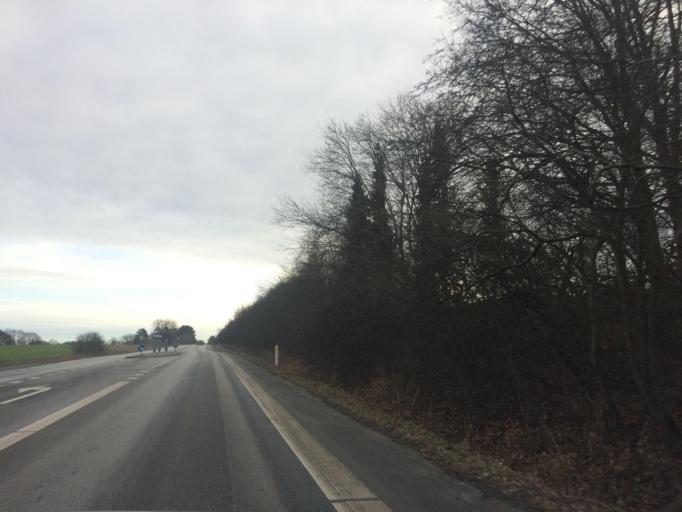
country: DK
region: Capital Region
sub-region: Fredensborg Kommune
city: Fredensborg
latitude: 55.9633
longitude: 12.4081
